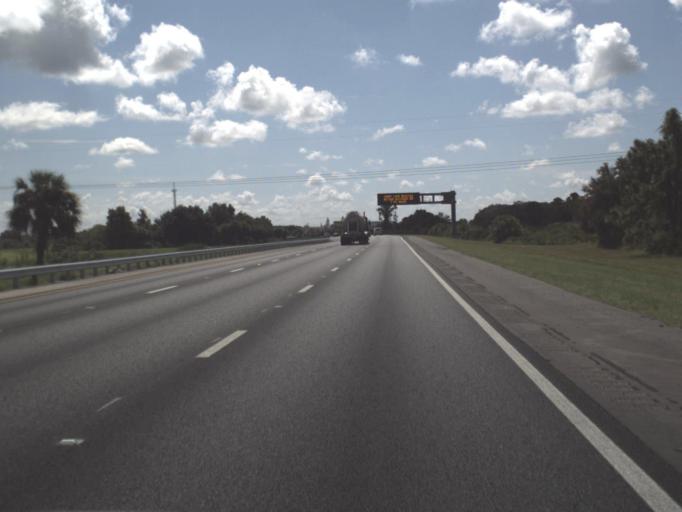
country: US
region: Florida
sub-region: Lee County
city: Suncoast Estates
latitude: 26.7277
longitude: -81.8372
